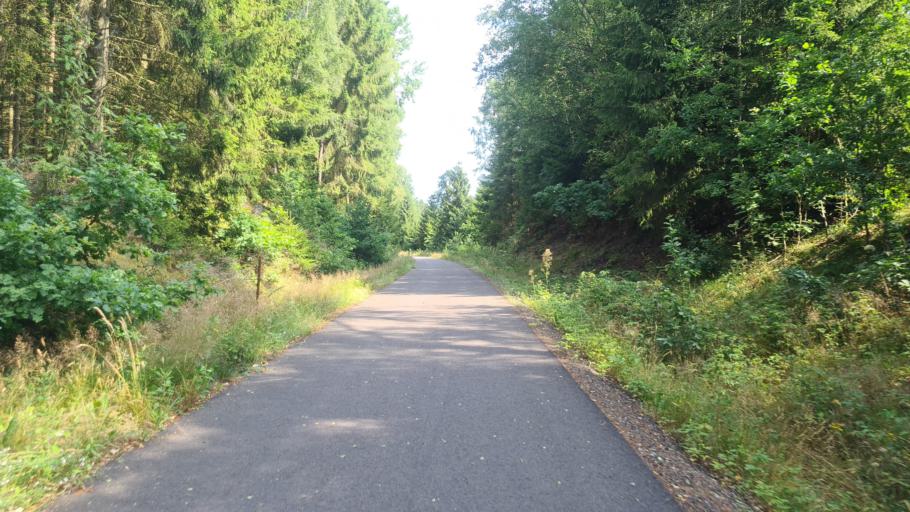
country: SE
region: Kronoberg
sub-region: Ljungby Kommun
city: Ljungby
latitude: 56.8591
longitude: 13.9767
